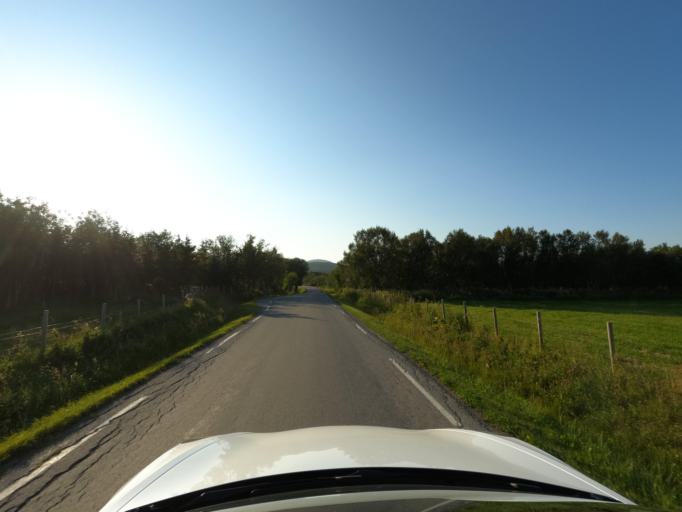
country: NO
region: Troms
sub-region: Skanland
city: Evenskjer
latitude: 68.4622
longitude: 16.6767
